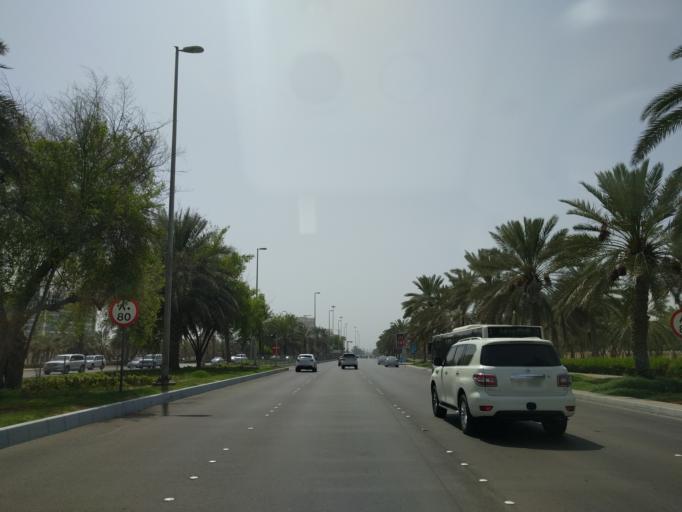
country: AE
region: Abu Dhabi
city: Abu Dhabi
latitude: 24.4360
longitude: 54.4211
